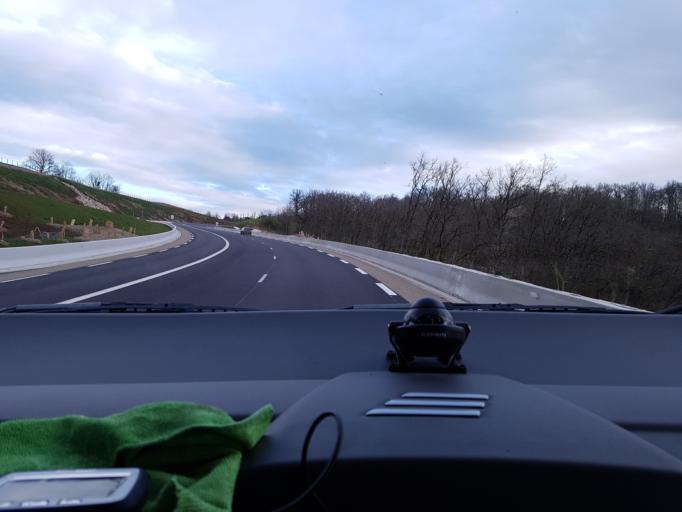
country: FR
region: Midi-Pyrenees
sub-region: Departement de l'Aveyron
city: Espalion
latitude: 44.5242
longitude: 2.7328
